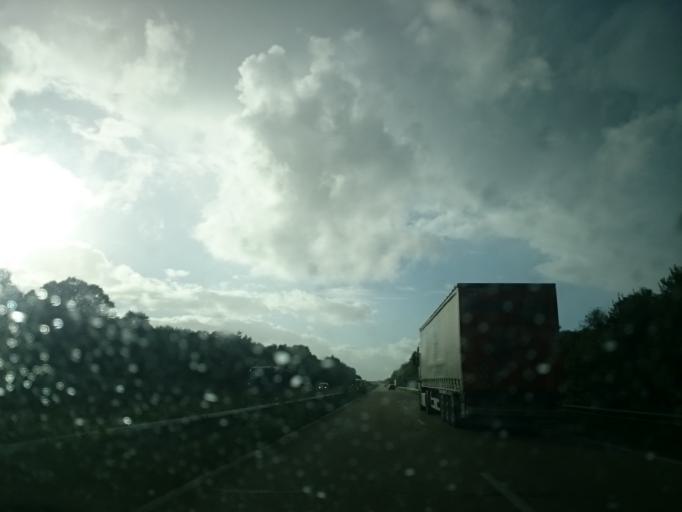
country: FR
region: Brittany
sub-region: Departement du Finistere
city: Plouigneau
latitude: 48.5766
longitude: -3.7286
